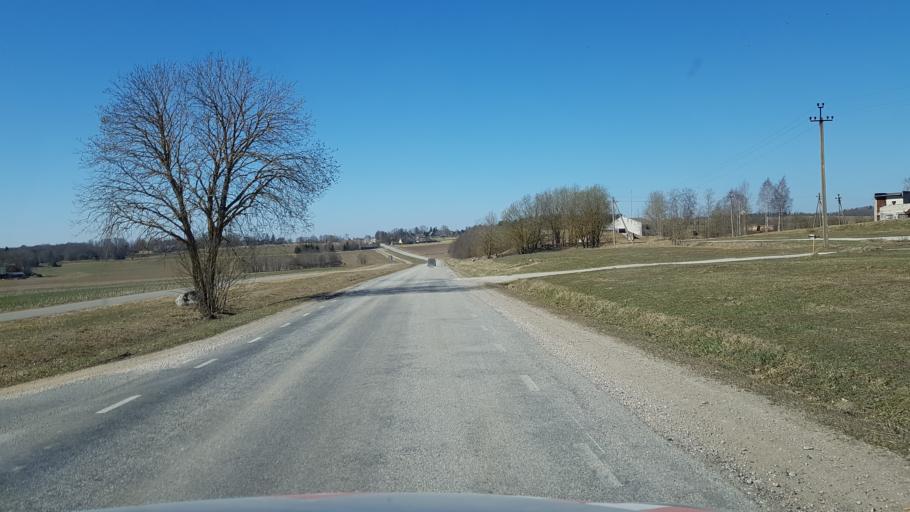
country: EE
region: Laeaene-Virumaa
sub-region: Vinni vald
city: Vinni
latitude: 59.0679
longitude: 26.5514
